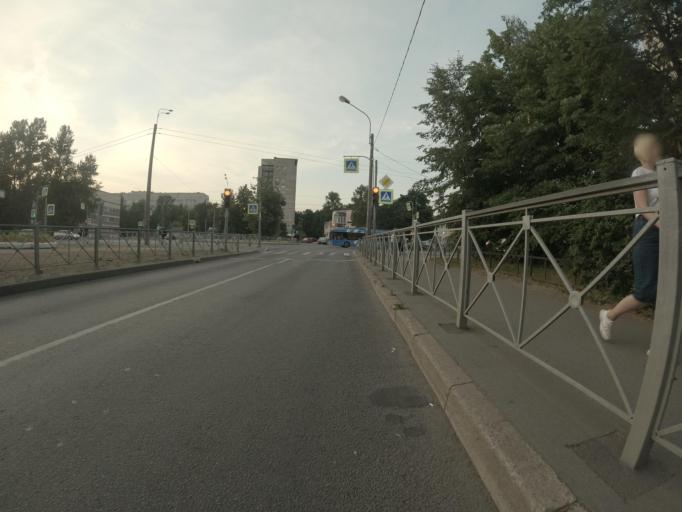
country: RU
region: Leningrad
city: Kalininskiy
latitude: 59.9850
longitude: 30.4119
